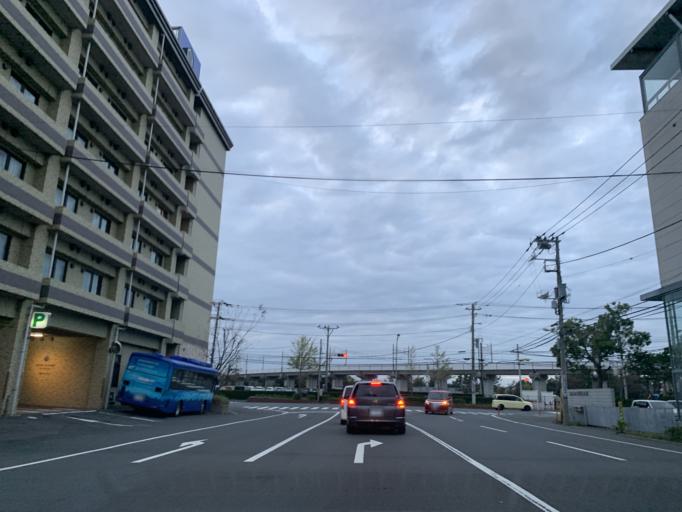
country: JP
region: Tokyo
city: Urayasu
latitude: 35.6329
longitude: 139.8929
